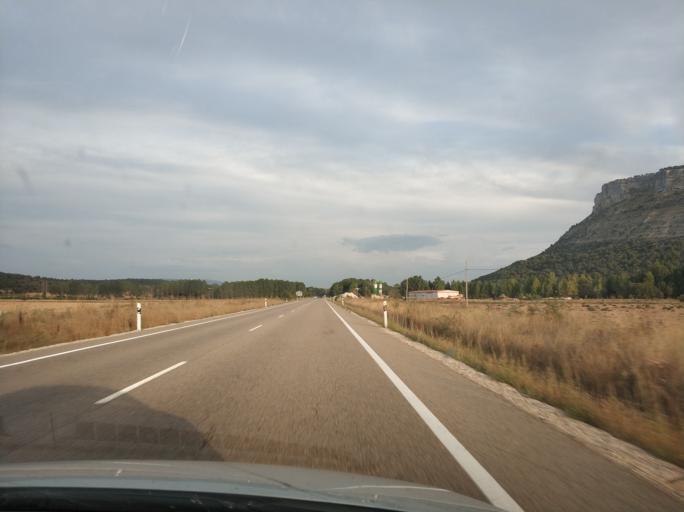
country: ES
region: Castille and Leon
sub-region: Provincia de Burgos
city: Hortiguela
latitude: 42.0642
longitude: -3.4141
